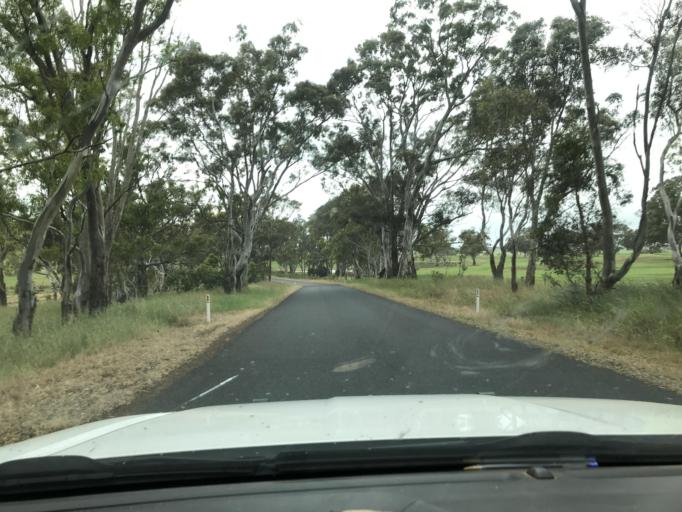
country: AU
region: Victoria
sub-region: Southern Grampians
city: Hamilton
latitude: -37.1903
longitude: 141.5480
